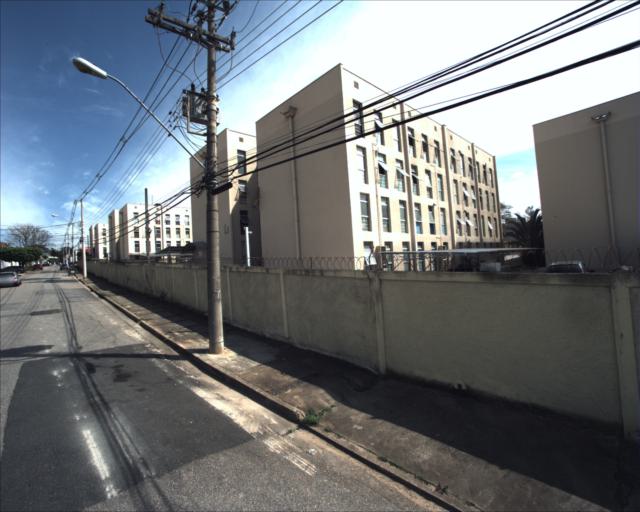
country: BR
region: Sao Paulo
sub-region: Sorocaba
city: Sorocaba
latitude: -23.5179
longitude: -47.5033
